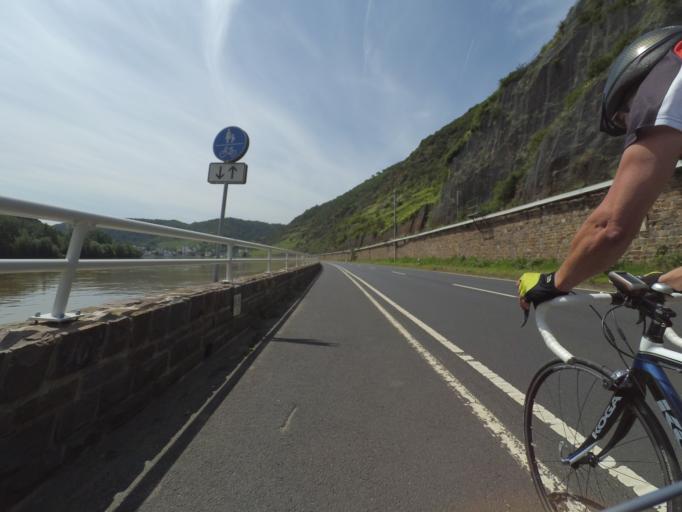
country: DE
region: Rheinland-Pfalz
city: Treis-Karden
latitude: 50.1869
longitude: 7.3148
